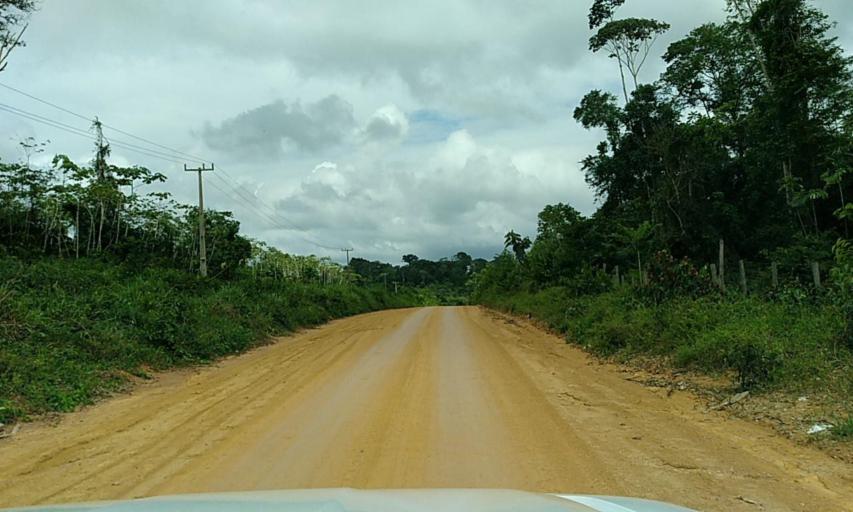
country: BR
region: Para
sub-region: Senador Jose Porfirio
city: Senador Jose Porfirio
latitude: -2.7583
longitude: -51.7927
